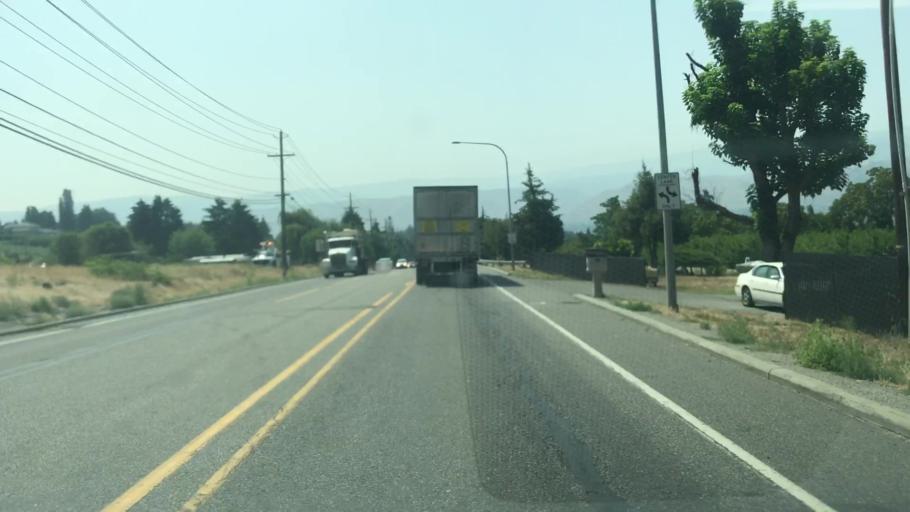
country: US
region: Washington
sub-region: Douglas County
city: East Wenatchee Bench
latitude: 47.4565
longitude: -120.2974
